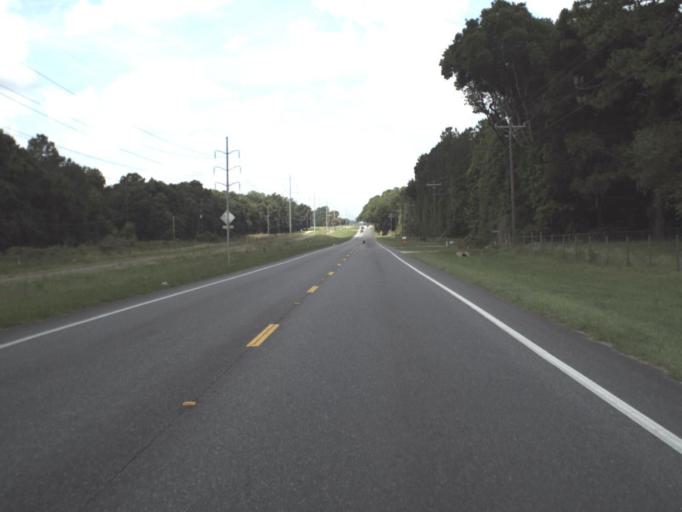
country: US
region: Florida
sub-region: Alachua County
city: Archer
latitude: 29.5751
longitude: -82.4631
